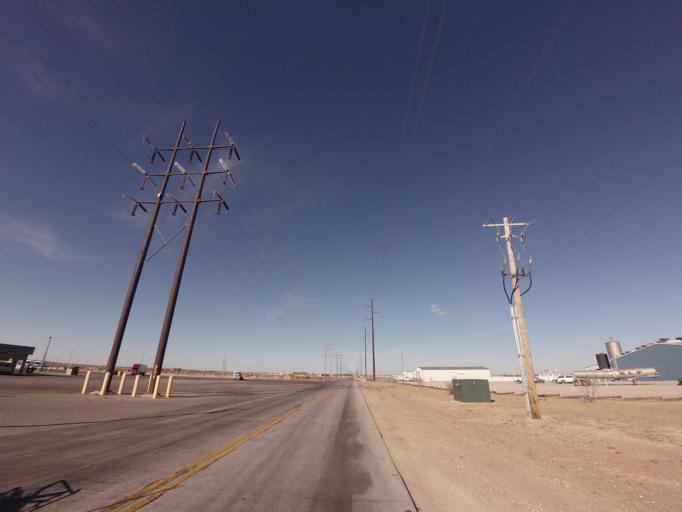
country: US
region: New Mexico
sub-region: Curry County
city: Clovis
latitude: 34.3943
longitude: -103.1432
